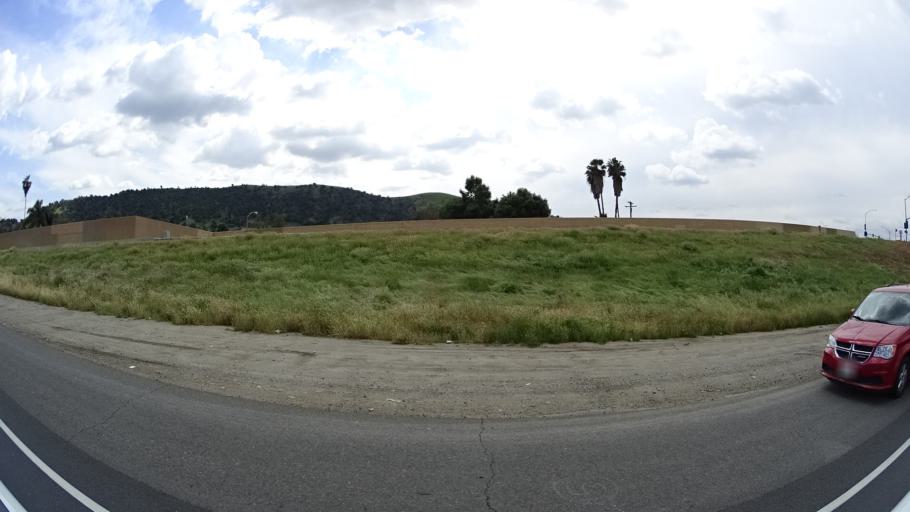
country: US
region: California
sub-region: Los Angeles County
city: Pomona
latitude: 34.0530
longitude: -117.7810
